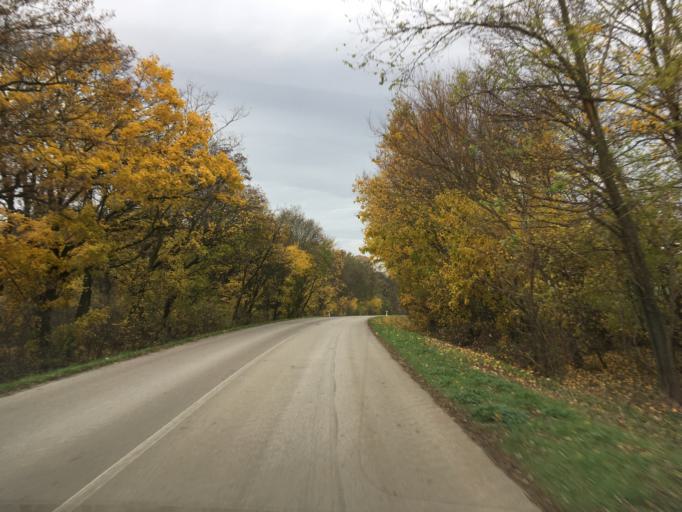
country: SK
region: Nitriansky
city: Svodin
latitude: 48.0304
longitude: 18.3935
